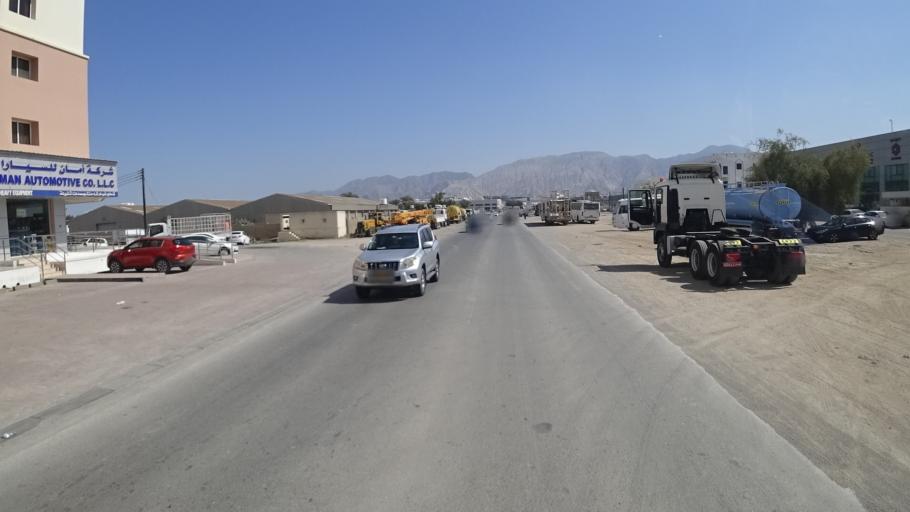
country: OM
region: Muhafazat Masqat
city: Bawshar
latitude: 23.5729
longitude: 58.3761
